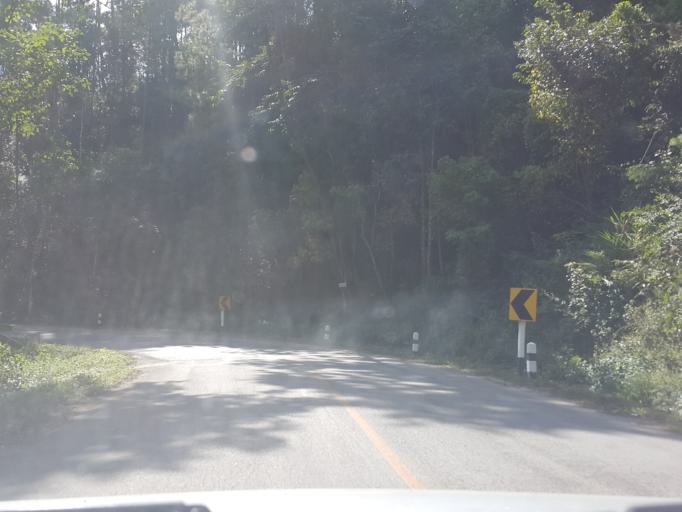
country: TH
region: Mae Hong Son
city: Mae Hi
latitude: 19.2513
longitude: 98.6423
